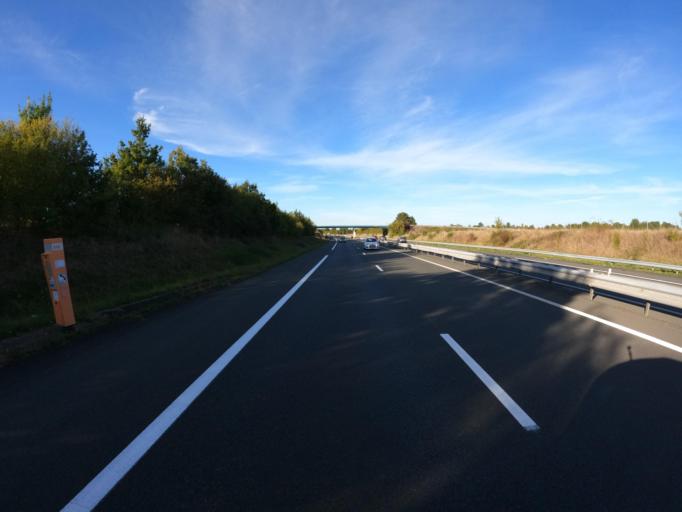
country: FR
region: Pays de la Loire
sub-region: Departement de Maine-et-Loire
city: Saint-Lambert-du-Lattay
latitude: 47.2655
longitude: -0.6146
